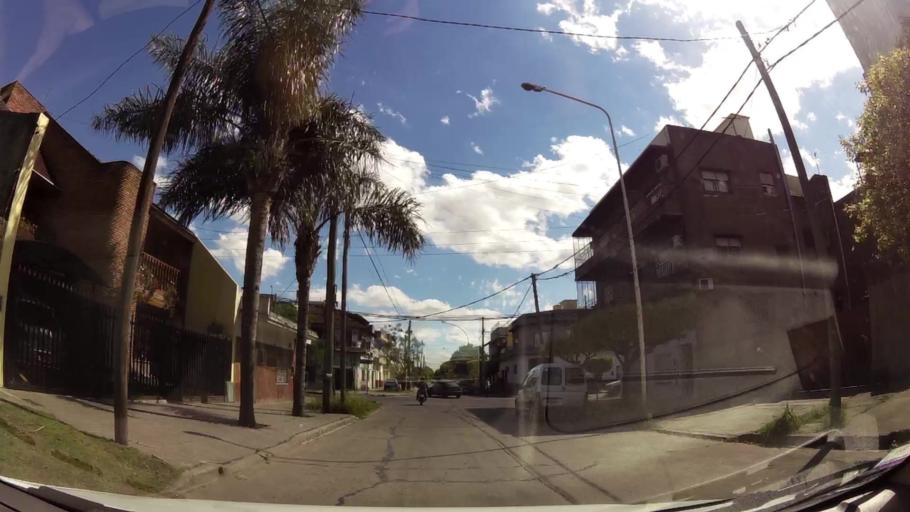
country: AR
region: Buenos Aires
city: San Justo
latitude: -34.6578
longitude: -58.5321
